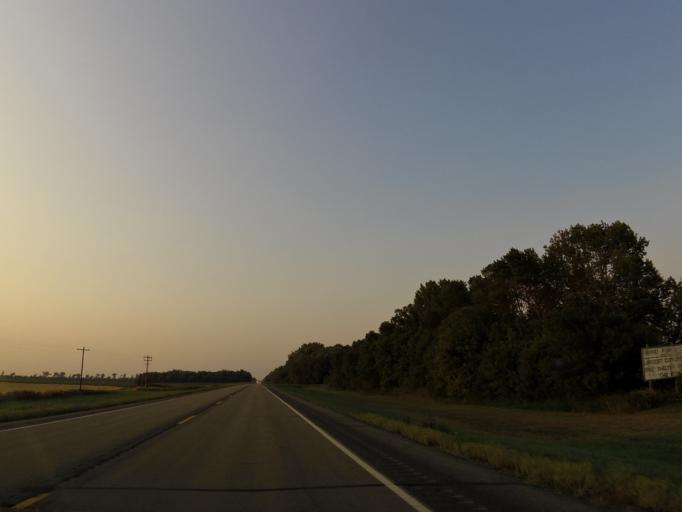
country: US
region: North Dakota
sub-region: Grand Forks County
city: Larimore
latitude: 47.8438
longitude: -97.6234
